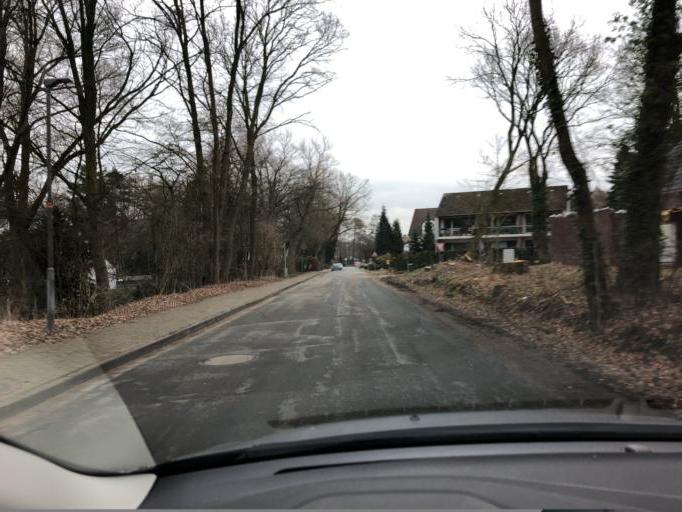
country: DE
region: Lower Saxony
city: Ganderkesee
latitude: 53.0909
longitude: 8.5619
